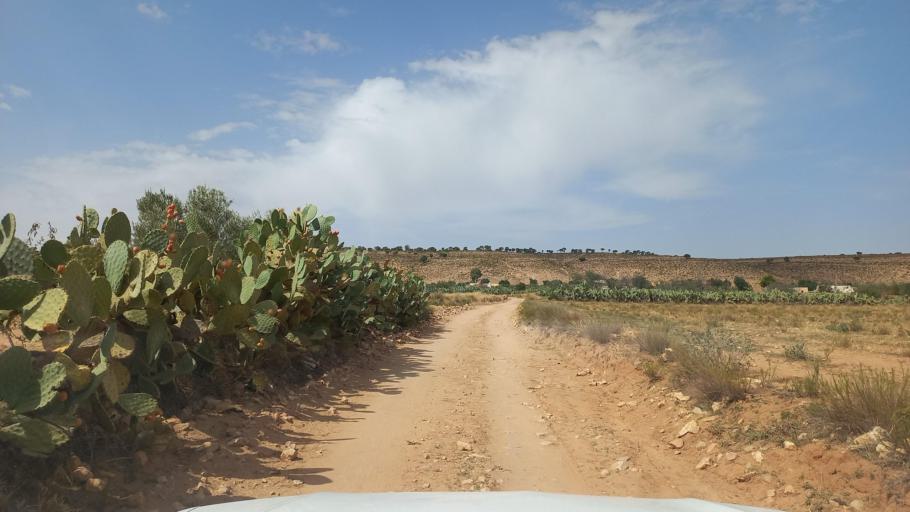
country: TN
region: Al Qasrayn
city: Kasserine
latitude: 35.3683
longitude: 8.8811
